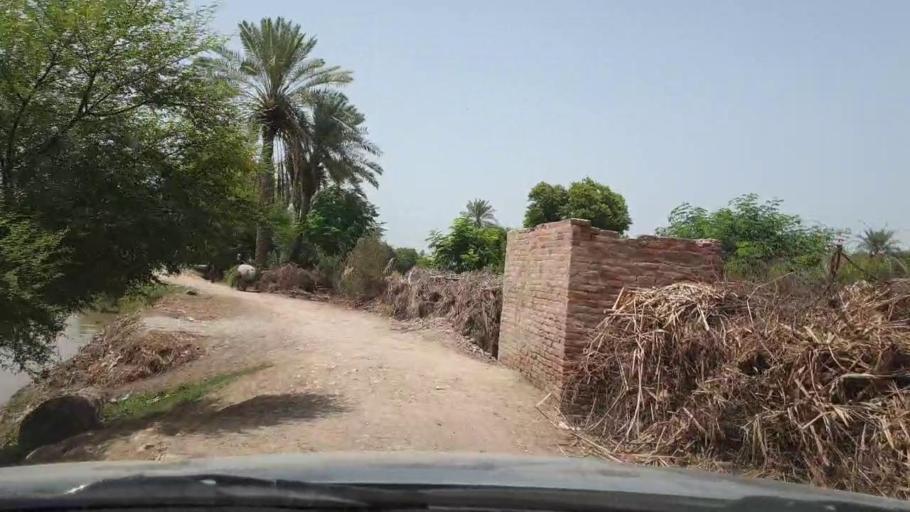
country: PK
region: Sindh
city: Pano Aqil
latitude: 27.9167
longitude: 69.1572
